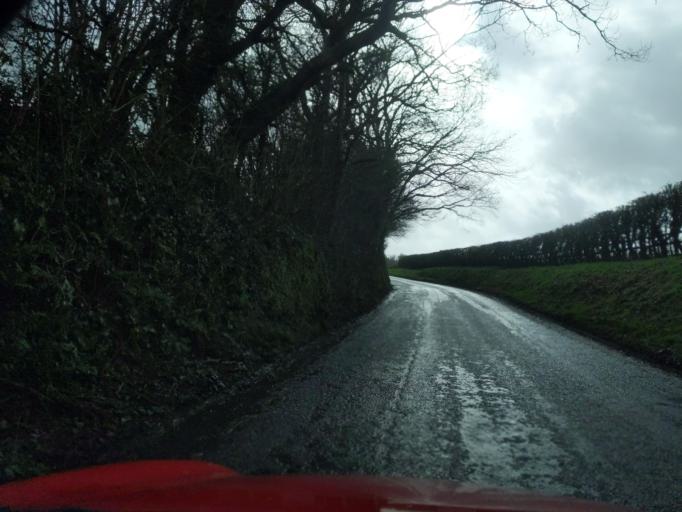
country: GB
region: England
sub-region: Devon
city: Ivybridge
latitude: 50.3818
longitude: -3.9362
